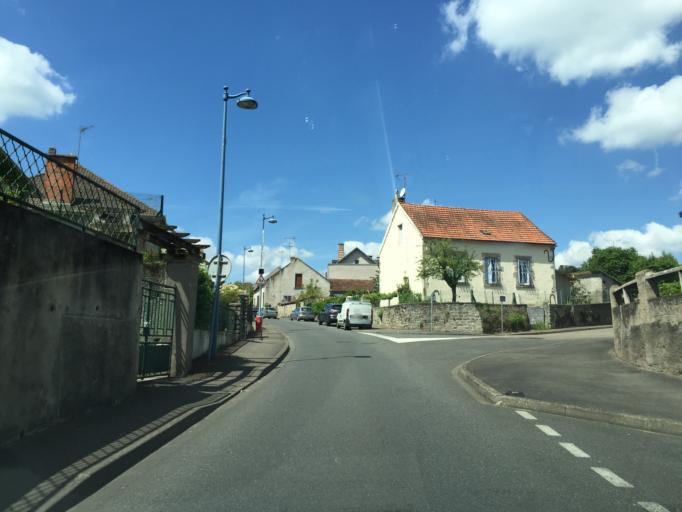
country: FR
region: Auvergne
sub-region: Departement de l'Allier
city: Bellerive-sur-Allier
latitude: 46.1172
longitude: 3.4056
